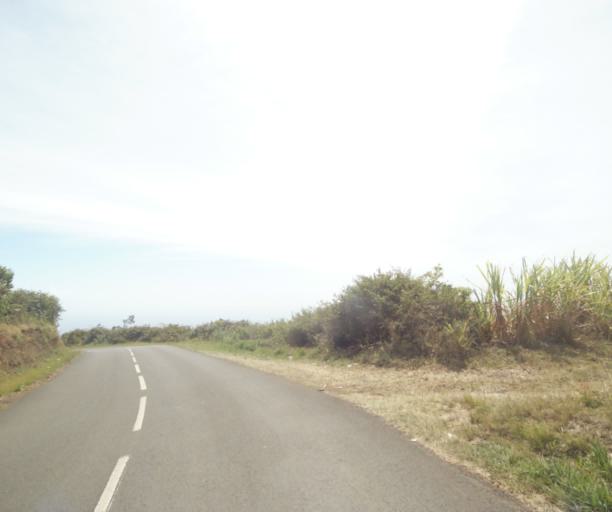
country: RE
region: Reunion
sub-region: Reunion
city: Trois-Bassins
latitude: -21.0724
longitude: 55.3041
